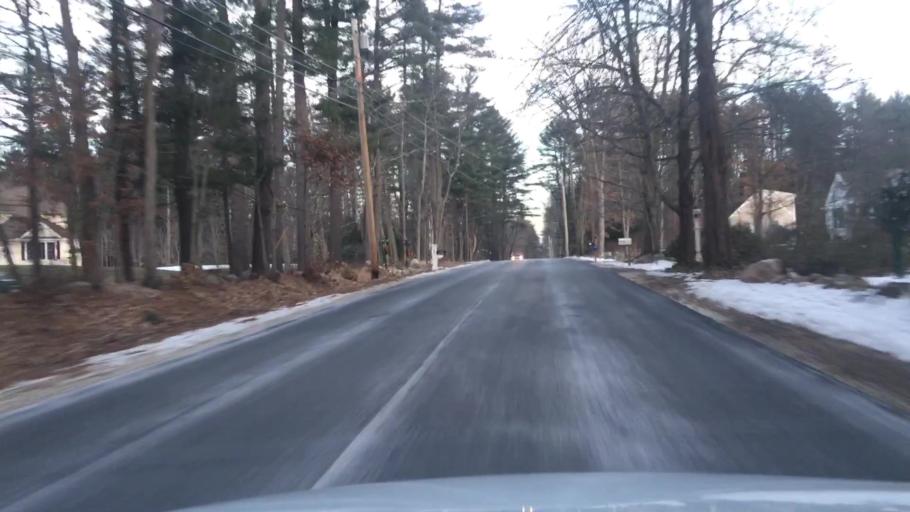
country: US
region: New Hampshire
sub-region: Strafford County
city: Rochester
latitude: 43.2673
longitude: -70.9348
